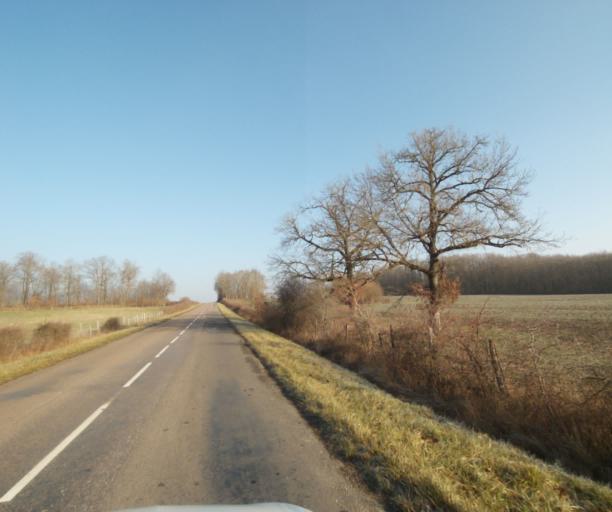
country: FR
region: Champagne-Ardenne
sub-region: Departement de la Haute-Marne
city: Montier-en-Der
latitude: 48.4297
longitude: 4.7512
